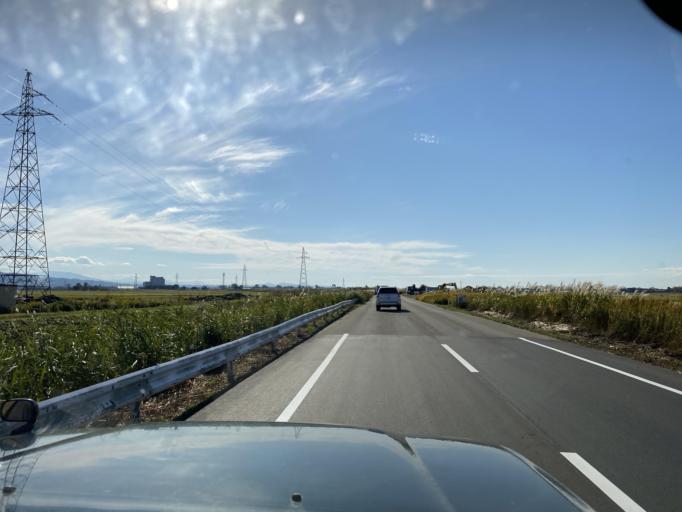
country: JP
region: Niigata
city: Niitsu-honcho
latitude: 37.8048
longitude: 139.0787
